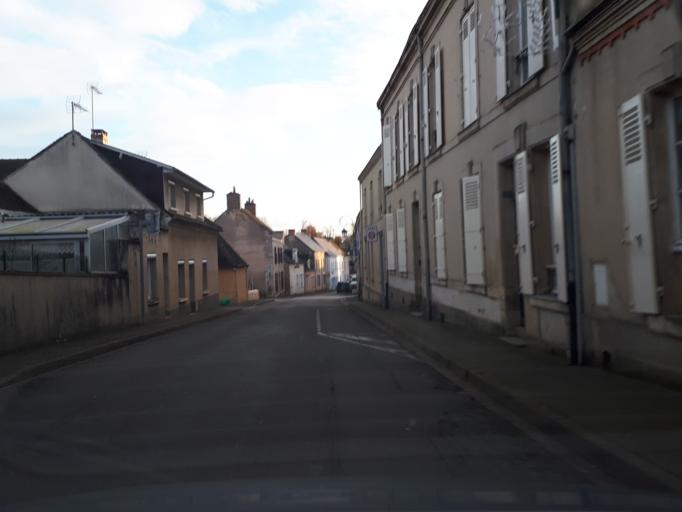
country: FR
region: Pays de la Loire
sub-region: Departement de la Sarthe
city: Souligne-sous-Ballon
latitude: 48.1387
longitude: 0.2369
